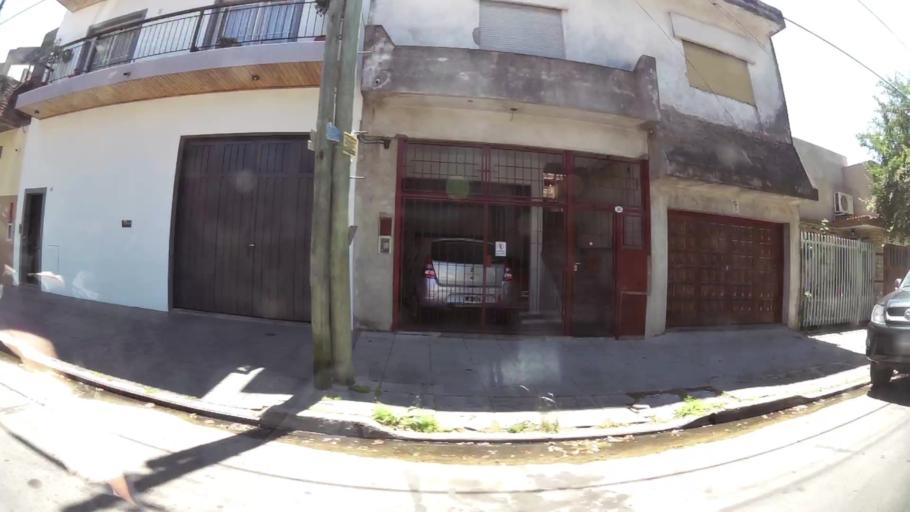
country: AR
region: Buenos Aires
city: Caseros
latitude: -34.5974
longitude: -58.5372
